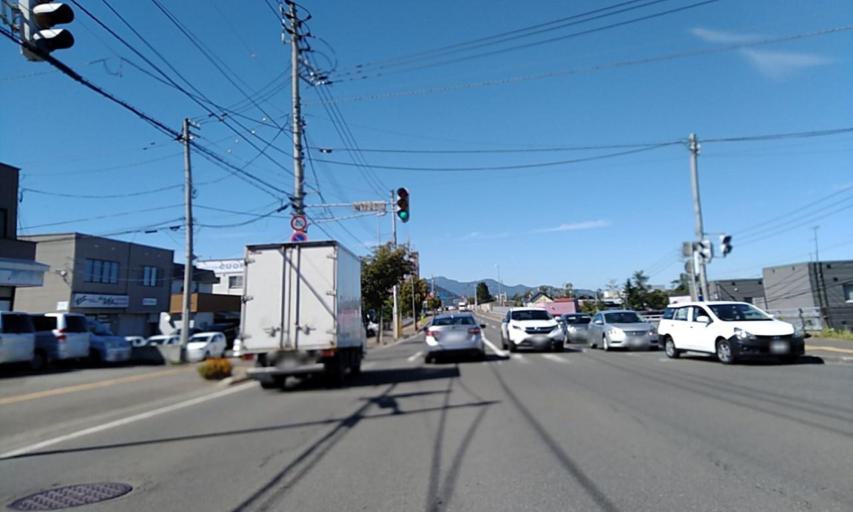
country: JP
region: Hokkaido
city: Sapporo
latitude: 43.0048
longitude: 141.3894
